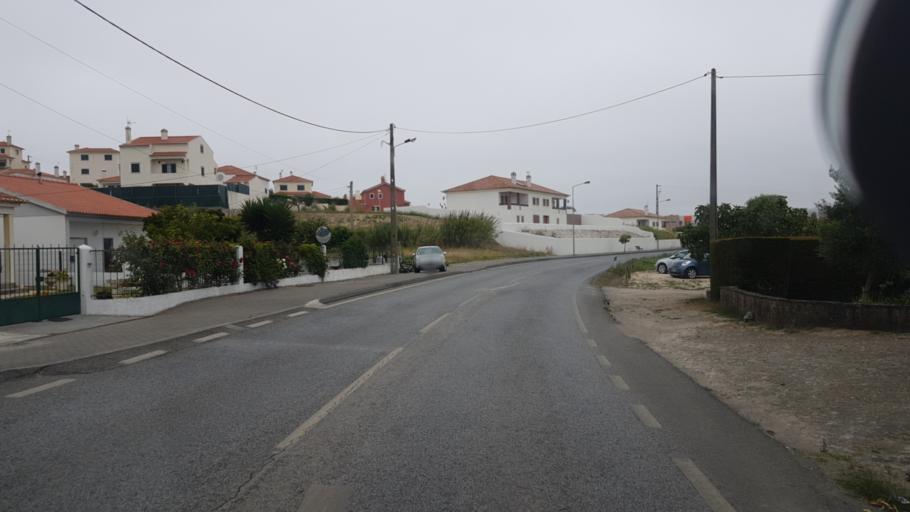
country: PT
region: Lisbon
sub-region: Torres Vedras
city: Silveira
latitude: 39.0929
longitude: -9.3262
